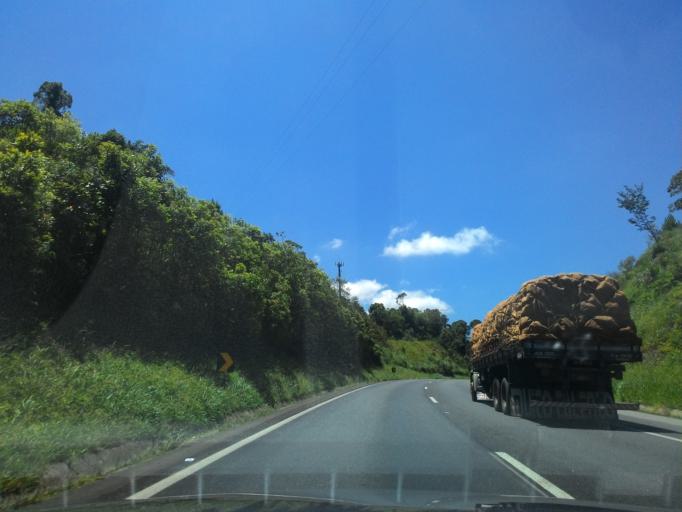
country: BR
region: Parana
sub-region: Antonina
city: Antonina
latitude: -25.0859
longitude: -48.6430
